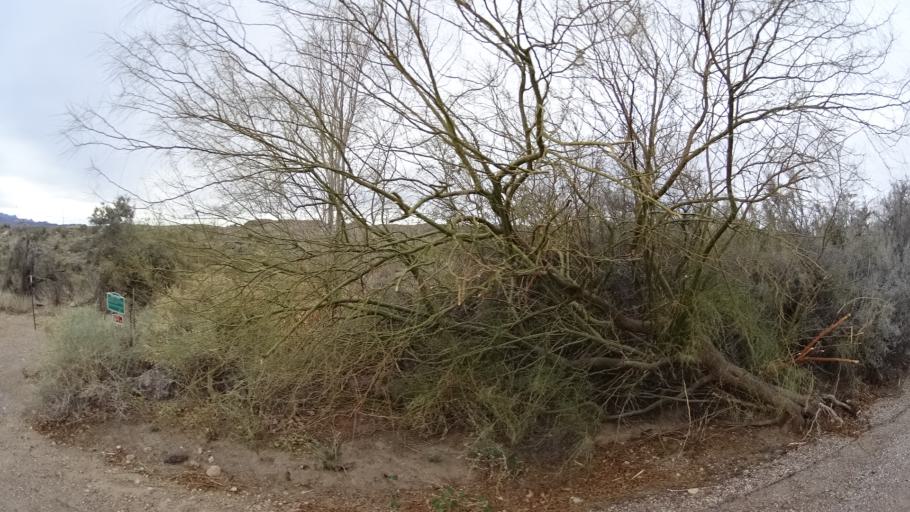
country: US
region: Arizona
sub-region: Mohave County
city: Kingman
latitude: 35.2027
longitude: -114.0759
